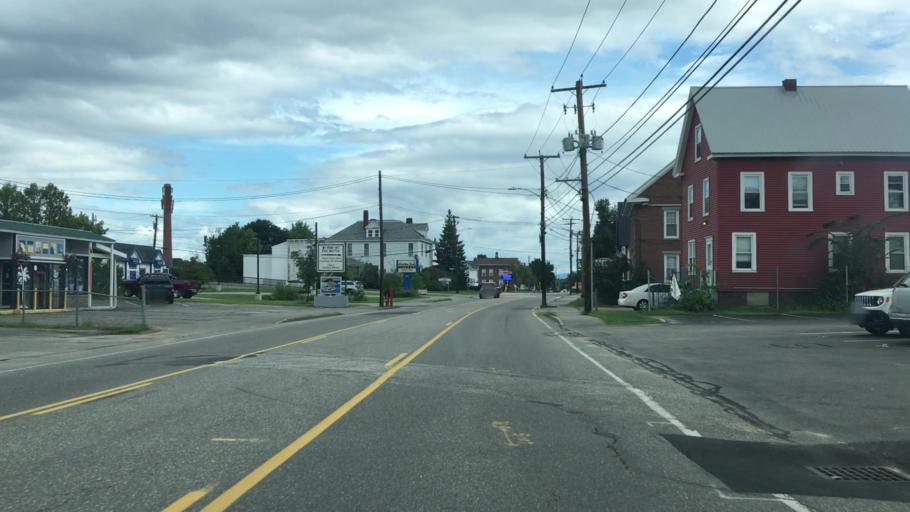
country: US
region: New Hampshire
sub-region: Belknap County
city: Laconia
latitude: 43.5437
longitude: -71.4650
